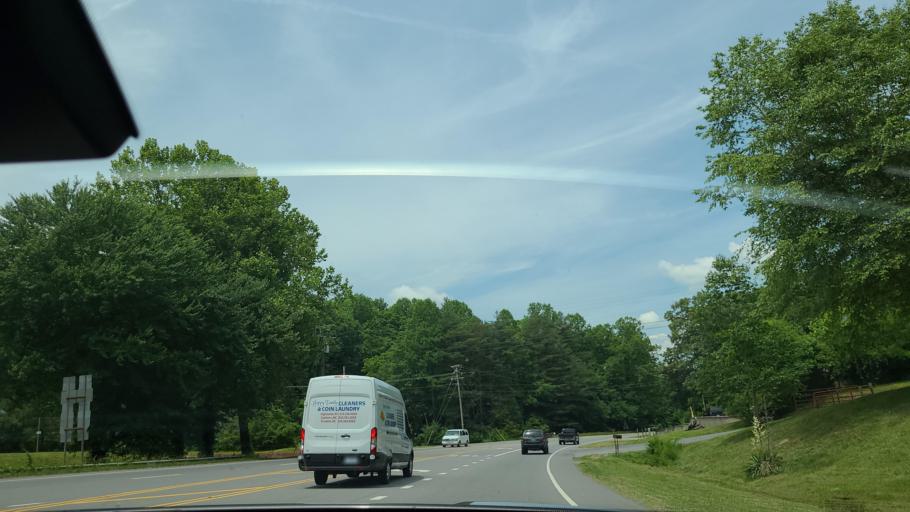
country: US
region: North Carolina
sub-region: Macon County
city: Franklin
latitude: 35.1748
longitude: -83.3611
